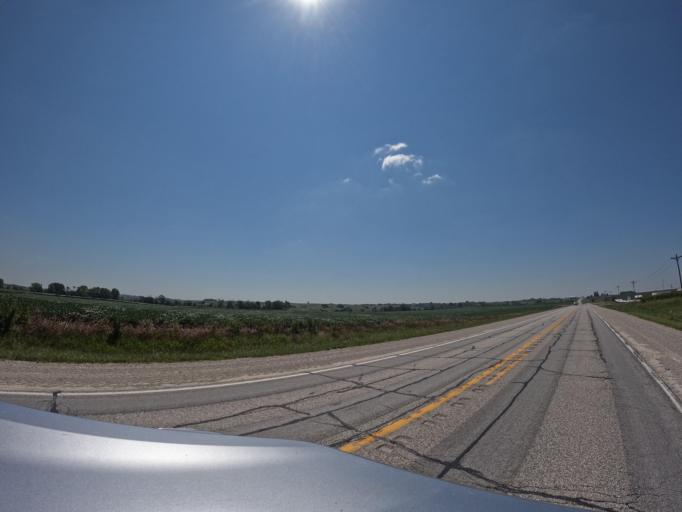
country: US
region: Iowa
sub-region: Keokuk County
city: Sigourney
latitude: 41.2896
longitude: -92.2046
